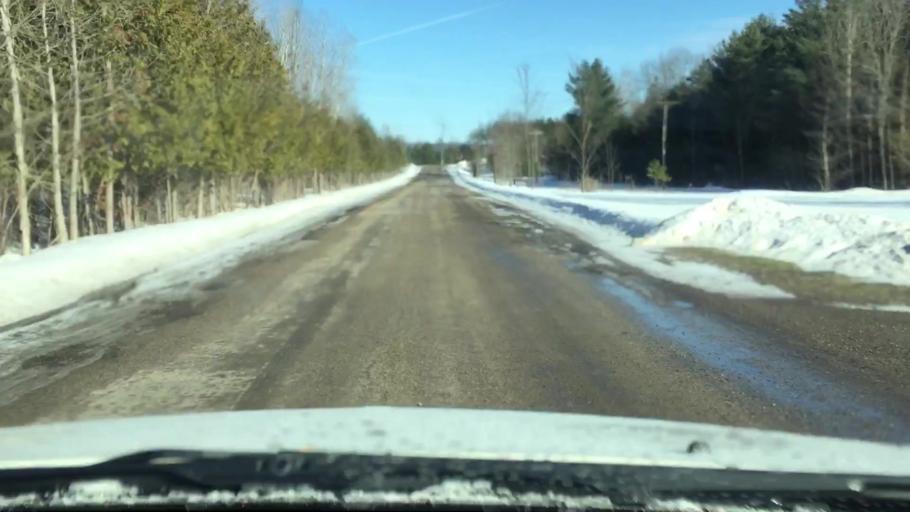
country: US
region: Michigan
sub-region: Charlevoix County
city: East Jordan
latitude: 45.1053
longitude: -85.1312
